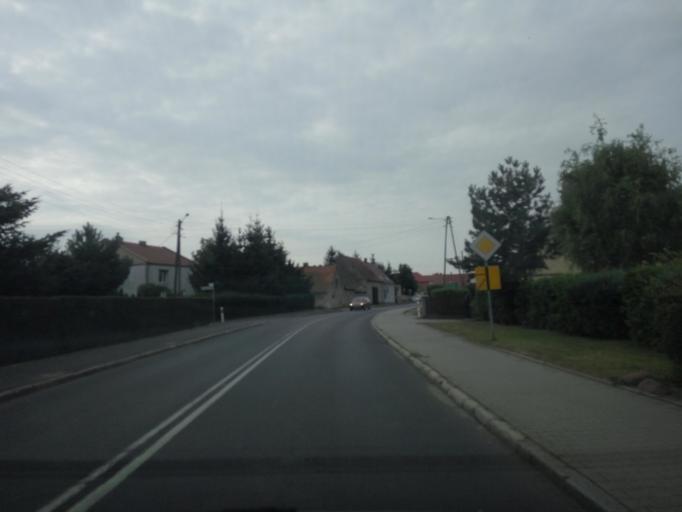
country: PL
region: Lower Silesian Voivodeship
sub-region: Powiat strzelinski
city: Strzelin
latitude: 50.8687
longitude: 17.0661
